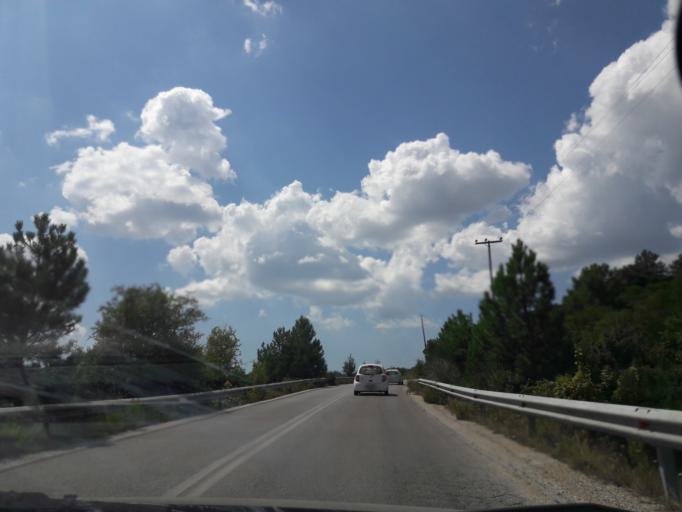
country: GR
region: Central Macedonia
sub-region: Nomos Chalkidikis
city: Polygyros
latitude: 40.3563
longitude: 23.4928
